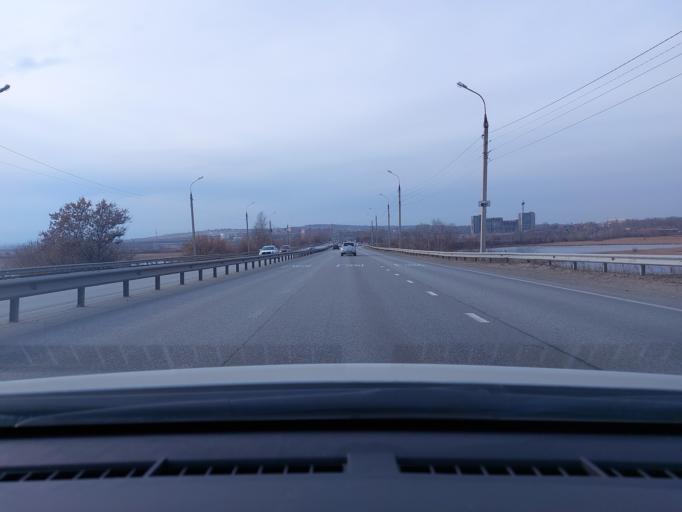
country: RU
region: Irkutsk
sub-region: Irkutskiy Rayon
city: Irkutsk
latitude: 52.3251
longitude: 104.2243
